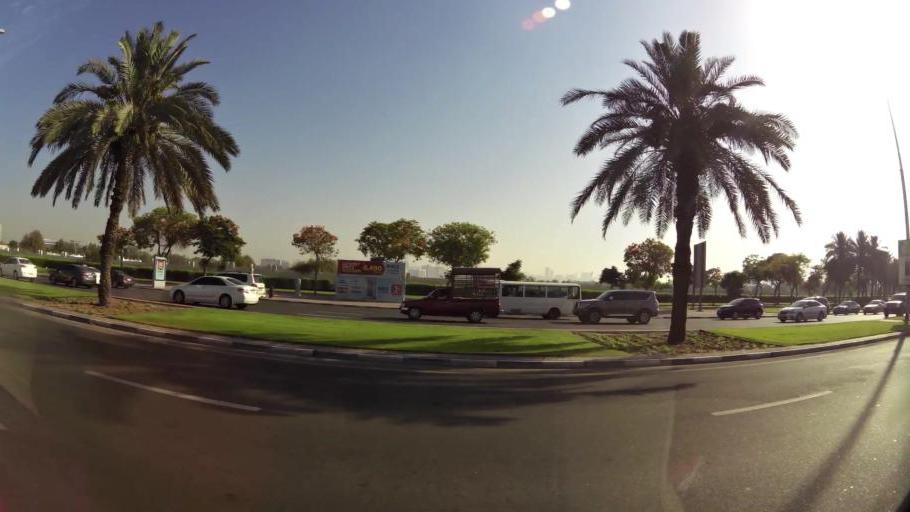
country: AE
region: Ash Shariqah
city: Sharjah
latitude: 25.2679
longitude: 55.3572
